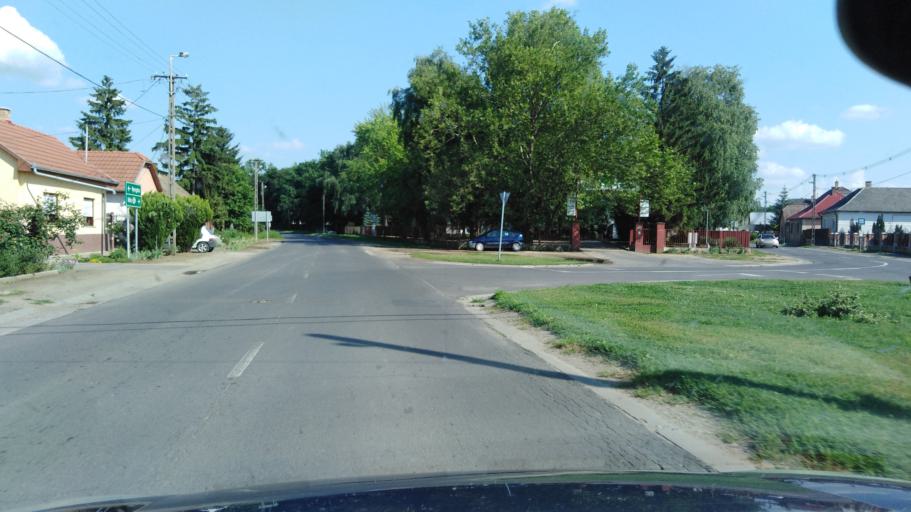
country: HU
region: Szabolcs-Szatmar-Bereg
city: Nyirbator
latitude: 47.8267
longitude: 22.1437
